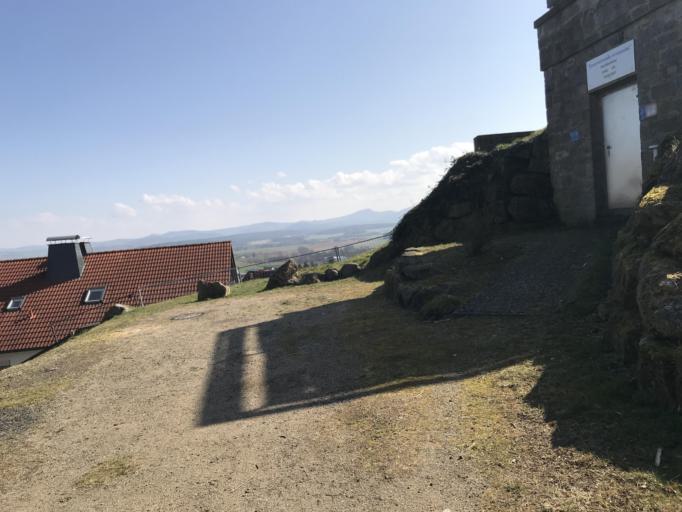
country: DE
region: Hesse
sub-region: Regierungsbezirk Kassel
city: Petersberg
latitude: 50.5618
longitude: 9.7116
